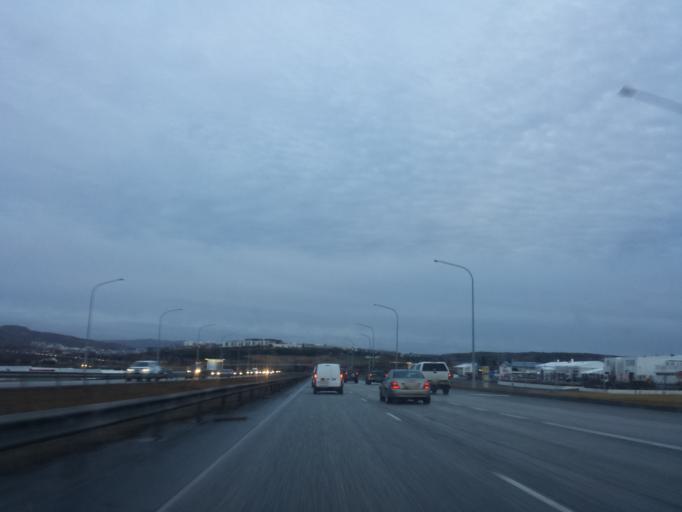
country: IS
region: Capital Region
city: Reykjavik
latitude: 64.1243
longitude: -21.7996
